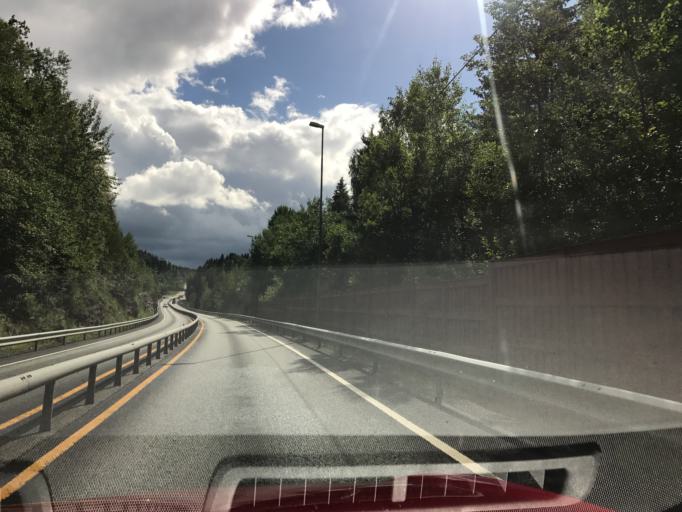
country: NO
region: Aust-Agder
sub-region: Gjerstad
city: Gjerstad
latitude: 58.8378
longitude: 9.0936
